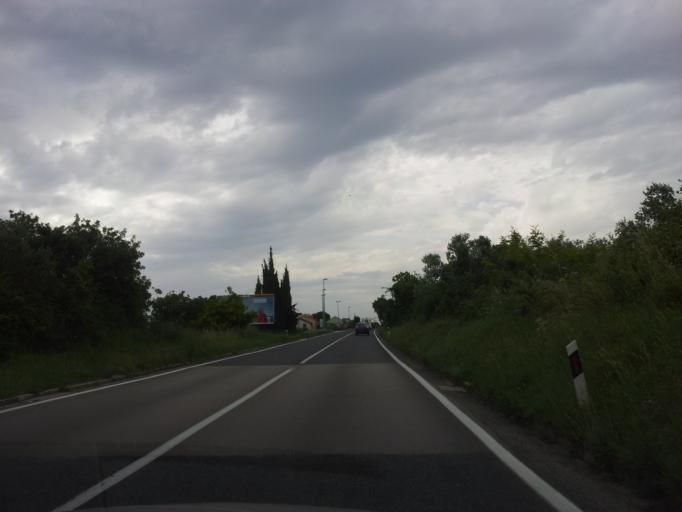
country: HR
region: Zadarska
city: Sveti Filip i Jakov
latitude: 43.9569
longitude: 15.4376
